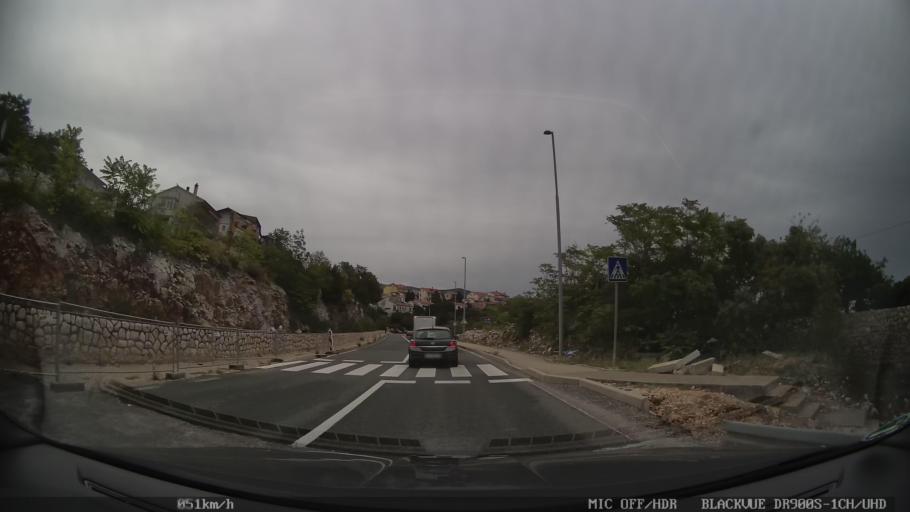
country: HR
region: Primorsko-Goranska
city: Novi Vinodolski
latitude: 45.1188
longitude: 14.8106
